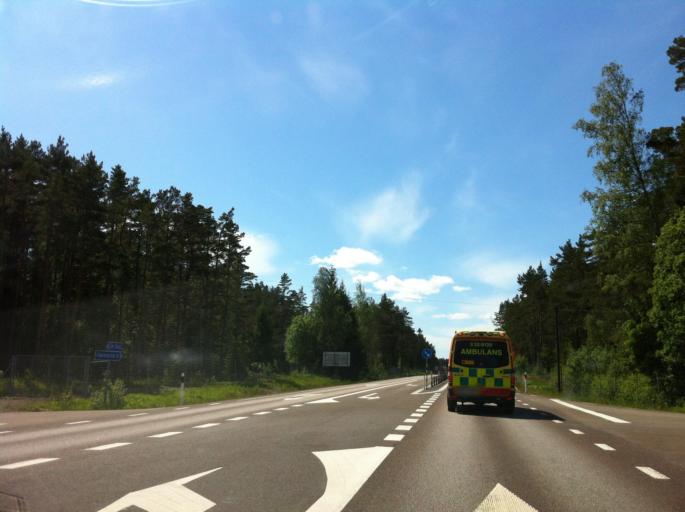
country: SE
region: Vaestra Goetaland
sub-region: Melleruds Kommun
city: Mellerud
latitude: 58.8309
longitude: 12.5322
